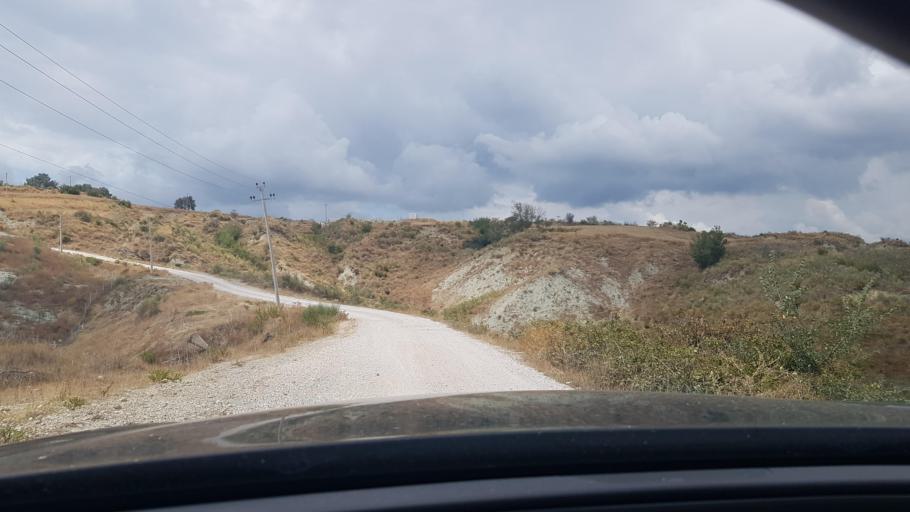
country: AL
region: Durres
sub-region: Rrethi i Durresit
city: Rrashbull
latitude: 41.2923
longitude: 19.5474
